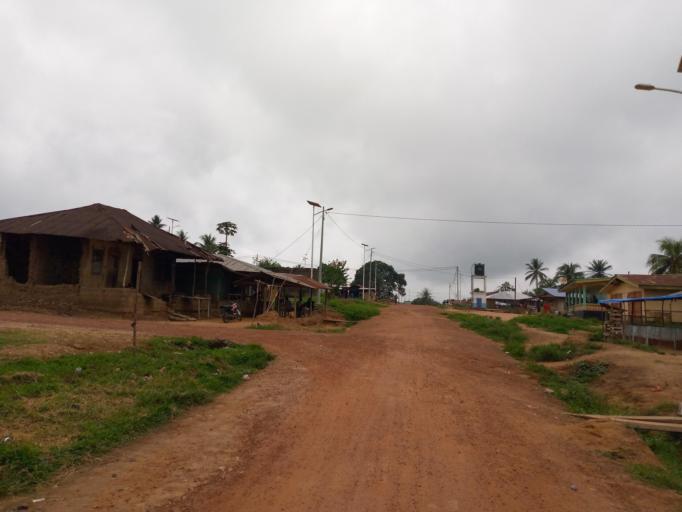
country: SL
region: Southern Province
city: Sumbuya
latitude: 7.5627
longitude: -12.0878
